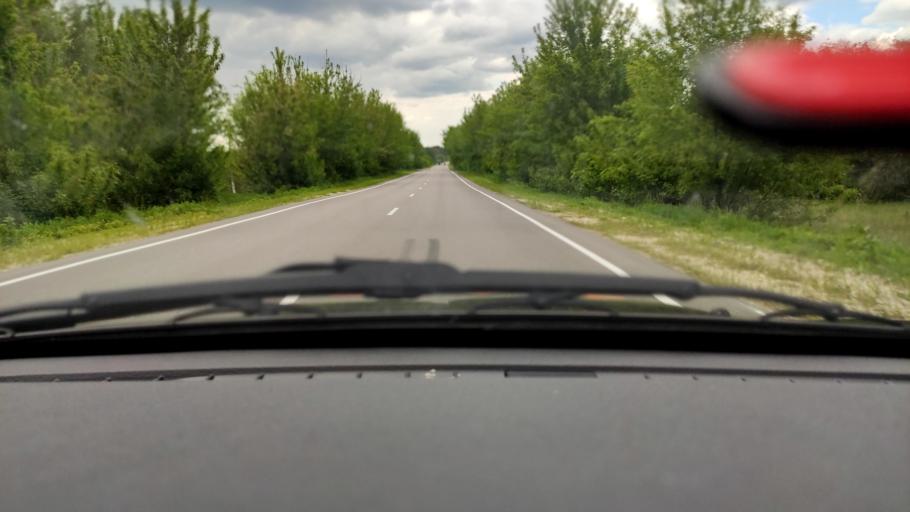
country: RU
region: Belgorod
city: Krasnoye
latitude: 51.0564
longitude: 38.8914
